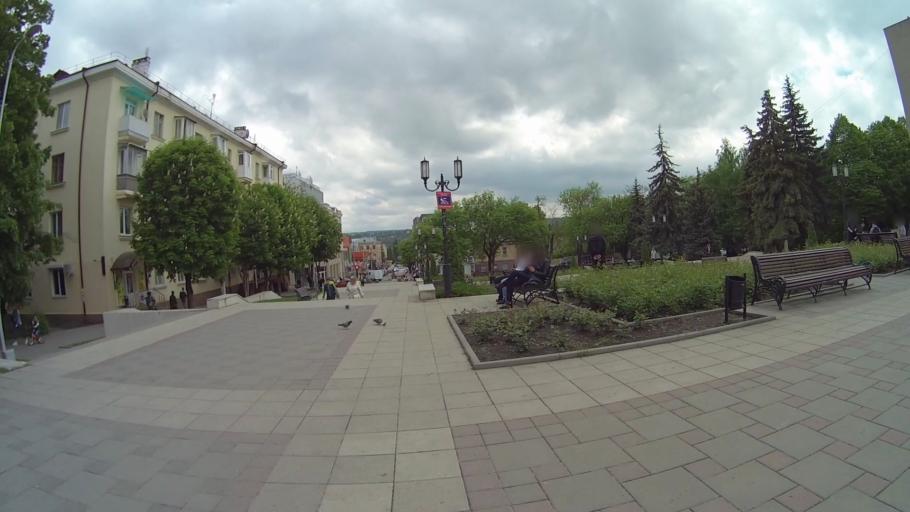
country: RU
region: Stavropol'skiy
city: Pyatigorsk
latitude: 44.0387
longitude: 43.0708
